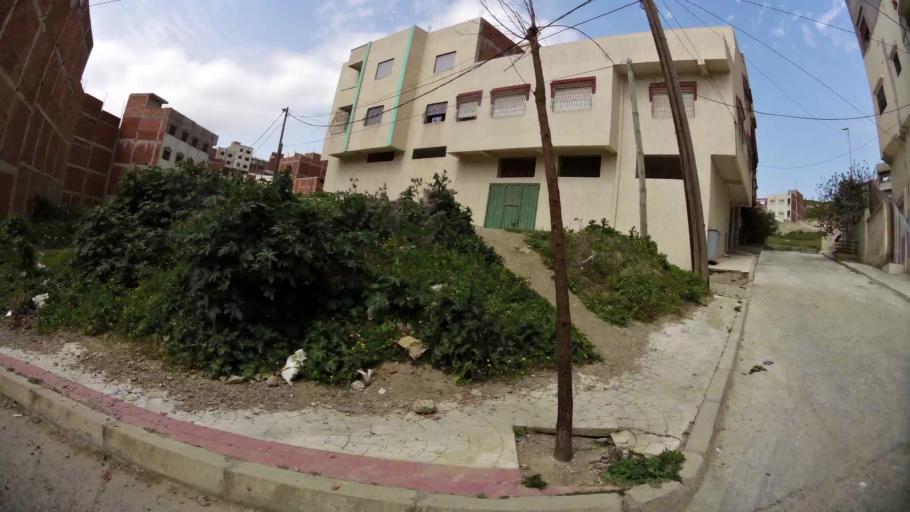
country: MA
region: Tanger-Tetouan
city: Tetouan
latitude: 35.5782
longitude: -5.3912
